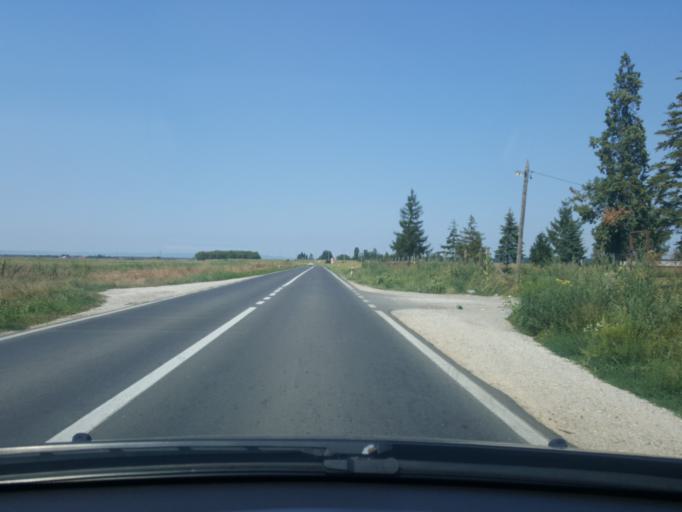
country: RS
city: Hrtkovci
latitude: 44.8485
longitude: 19.7693
